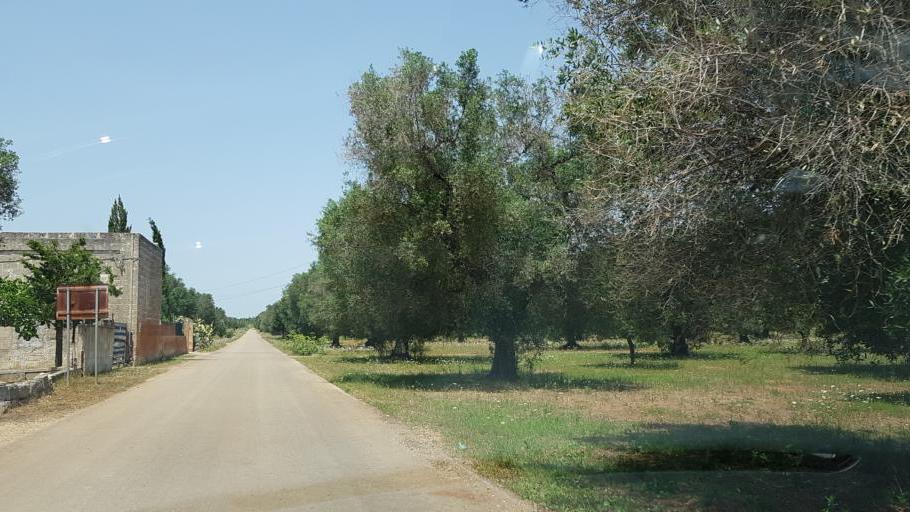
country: IT
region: Apulia
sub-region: Provincia di Lecce
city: Porto Cesareo
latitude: 40.3192
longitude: 17.8946
